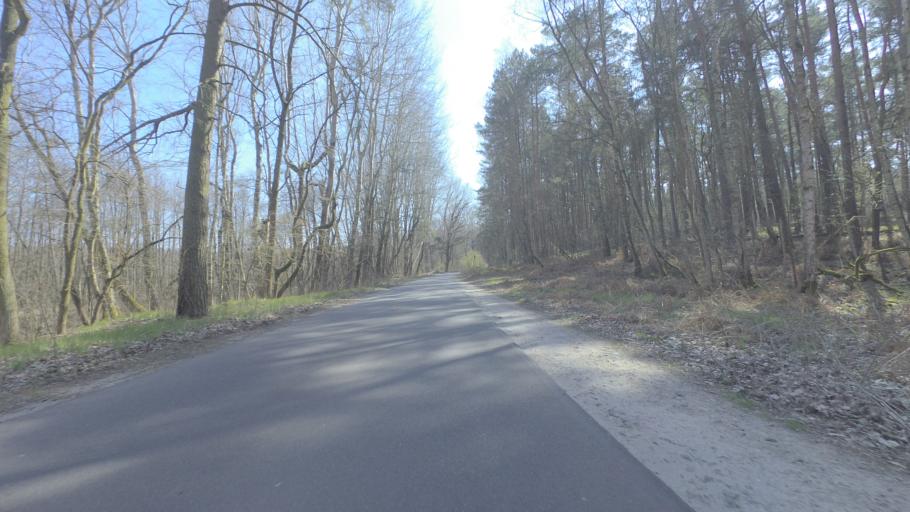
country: DE
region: Brandenburg
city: Bestensee
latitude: 52.2081
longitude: 13.6145
